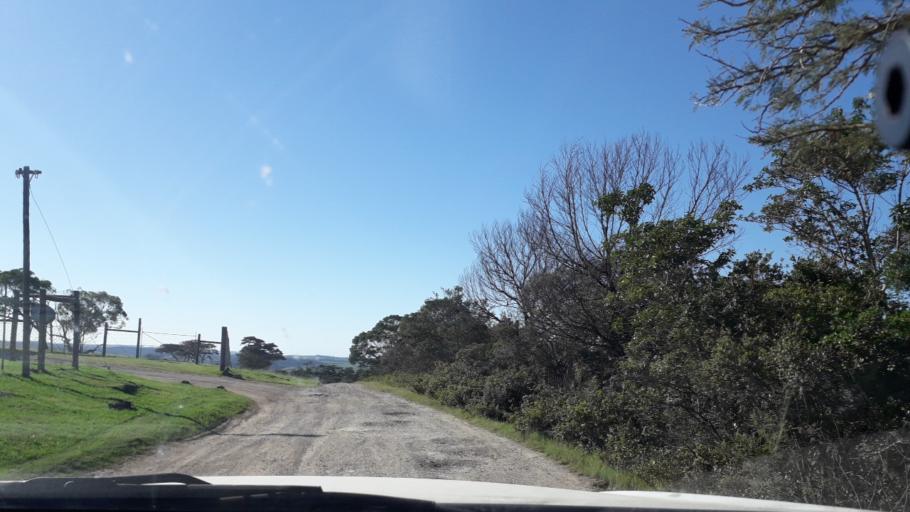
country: ZA
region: Eastern Cape
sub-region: Buffalo City Metropolitan Municipality
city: East London
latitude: -32.8413
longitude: 27.9760
